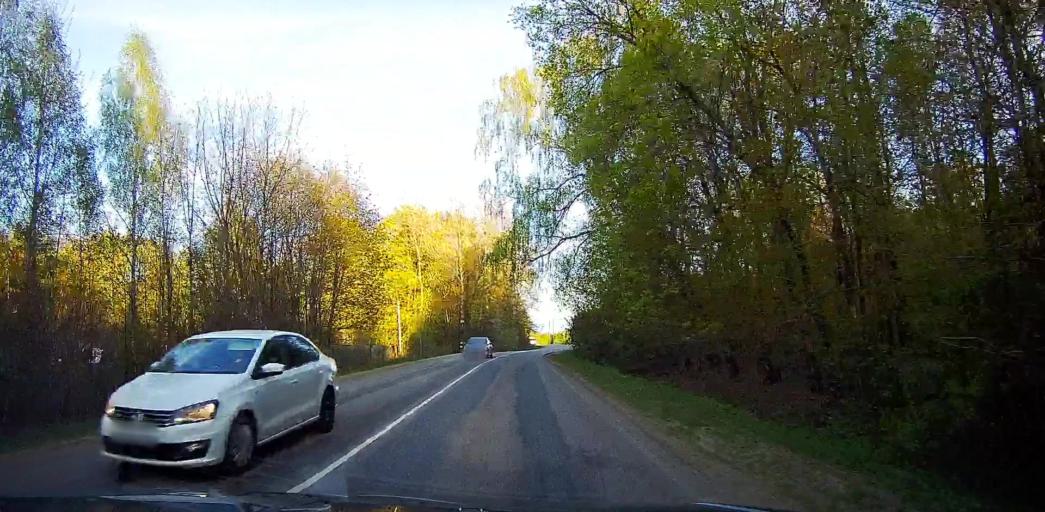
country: RU
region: Moskovskaya
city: Meshcherino
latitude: 55.2517
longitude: 38.2815
